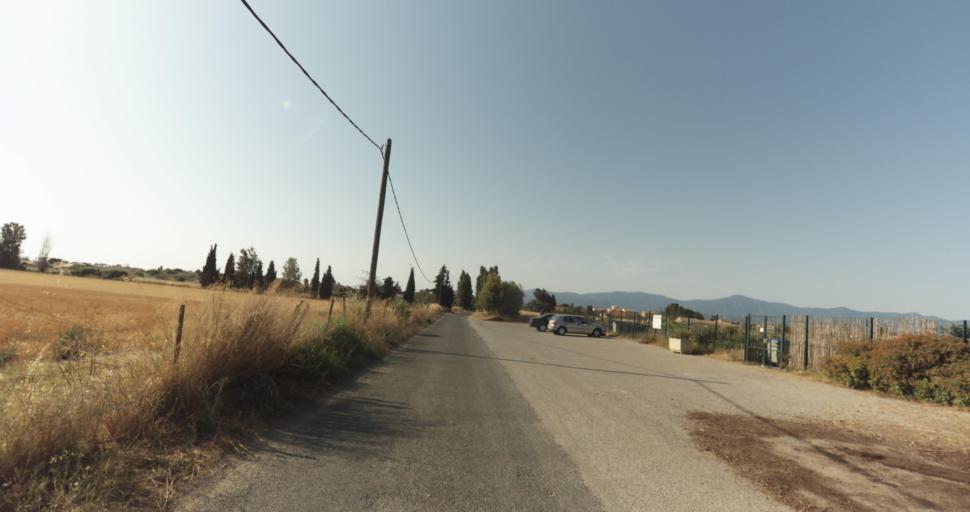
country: FR
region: Languedoc-Roussillon
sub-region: Departement des Pyrenees-Orientales
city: Alenya
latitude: 42.6465
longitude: 2.9766
